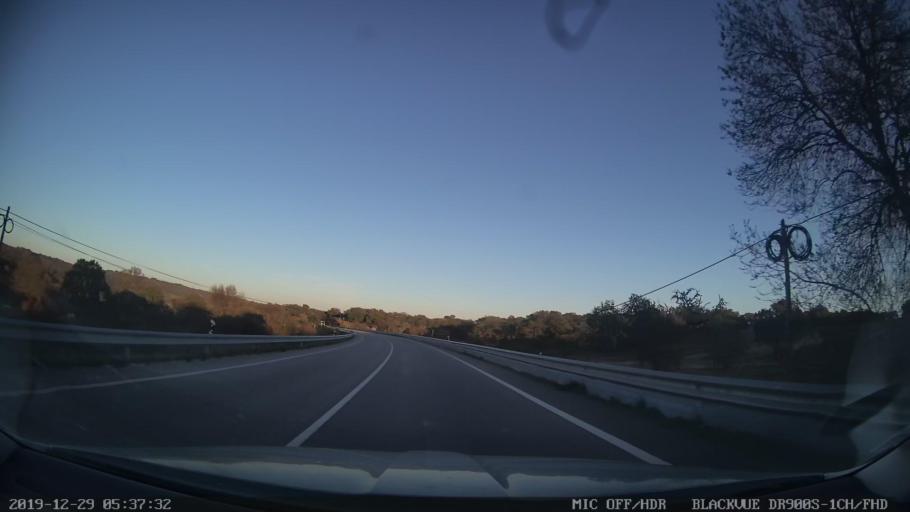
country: PT
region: Guarda
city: Alcains
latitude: 39.9703
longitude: -7.3560
